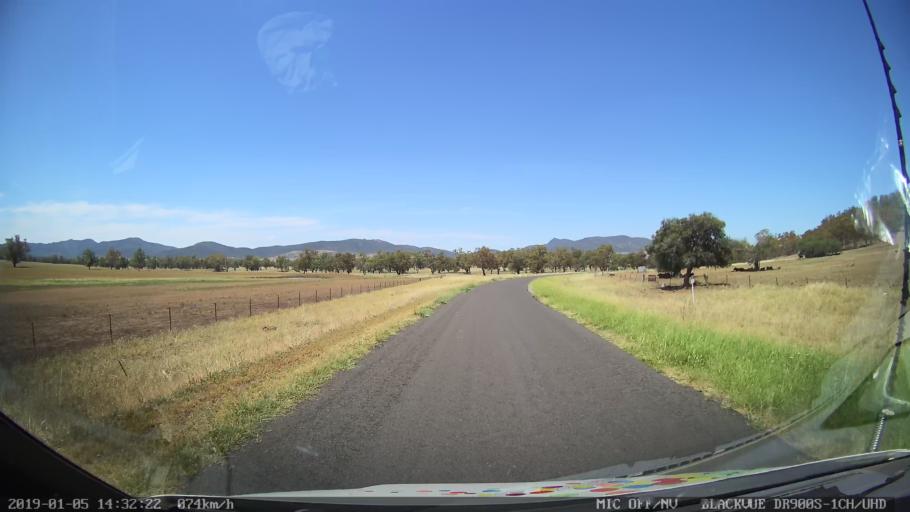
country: AU
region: New South Wales
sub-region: Tamworth Municipality
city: Phillip
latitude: -31.2210
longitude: 150.6172
